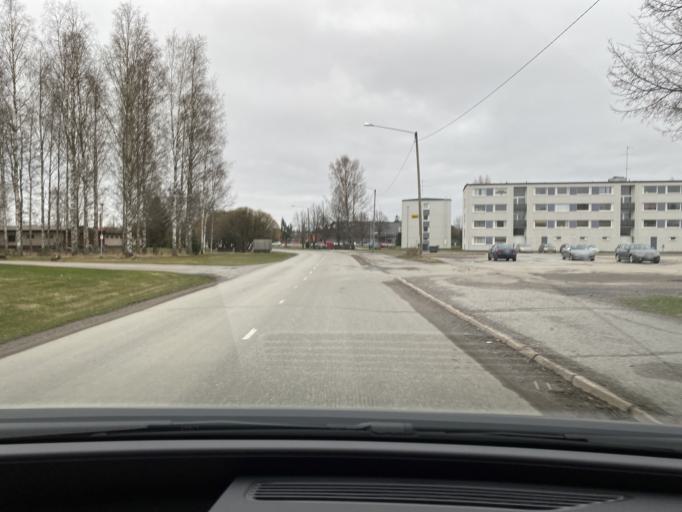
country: FI
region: Satakunta
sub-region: Pori
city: Huittinen
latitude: 61.1874
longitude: 22.6982
